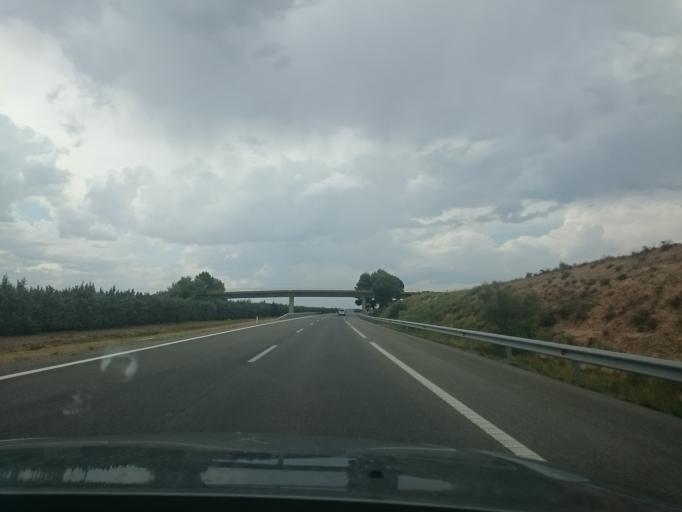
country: ES
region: Navarre
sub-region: Provincia de Navarra
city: Murchante
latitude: 42.0436
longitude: -1.6603
